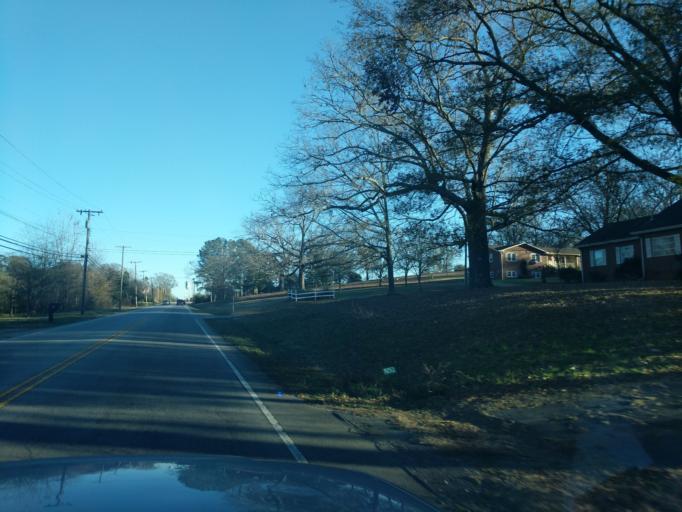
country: US
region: South Carolina
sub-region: Oconee County
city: Westminster
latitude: 34.6729
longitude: -83.1091
